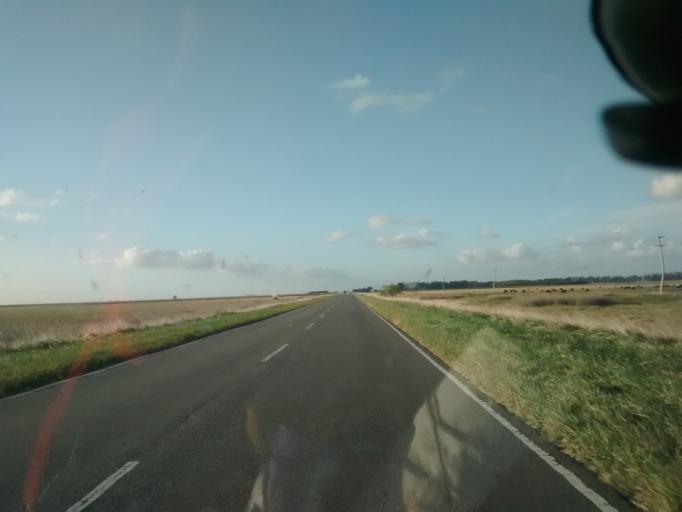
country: AR
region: Buenos Aires
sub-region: Partido de General Belgrano
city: General Belgrano
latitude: -36.0589
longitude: -58.6254
